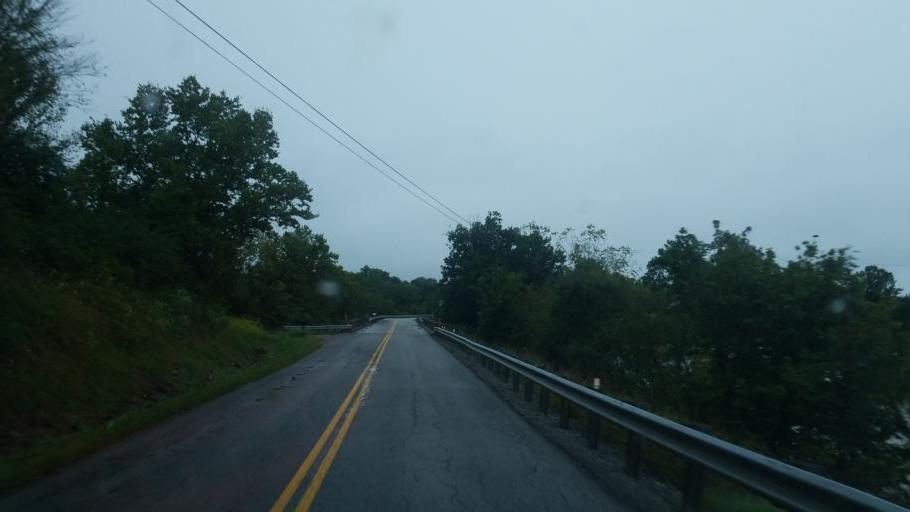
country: US
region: Kentucky
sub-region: Fleming County
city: Flemingsburg
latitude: 38.4147
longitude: -83.6920
